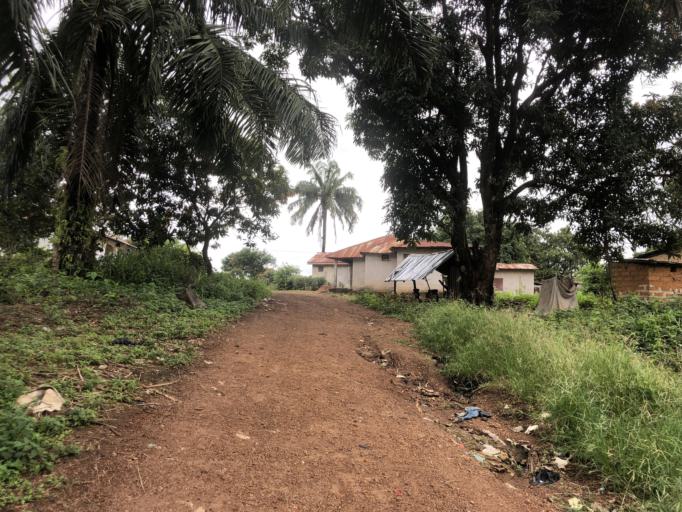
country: SL
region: Northern Province
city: Makeni
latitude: 8.9067
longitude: -12.0420
